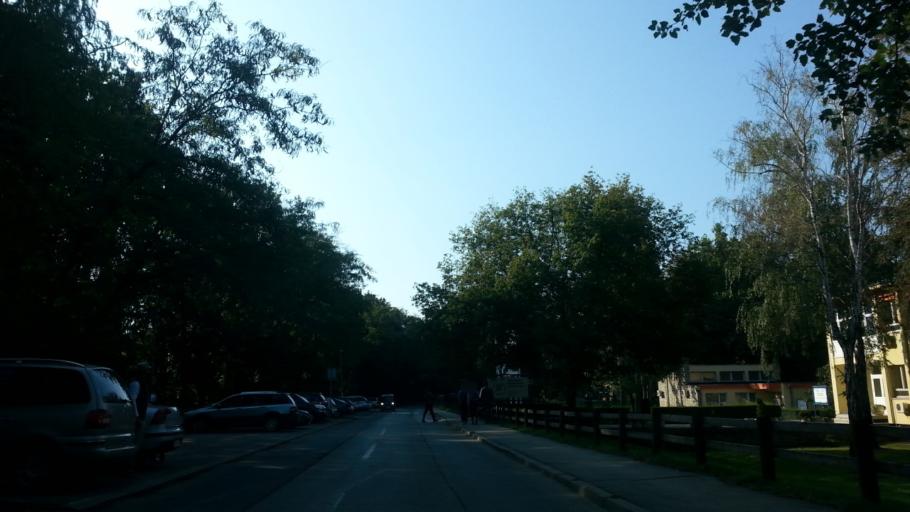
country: RS
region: Central Serbia
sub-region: Belgrade
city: Cukarica
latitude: 44.7652
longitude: 20.4296
